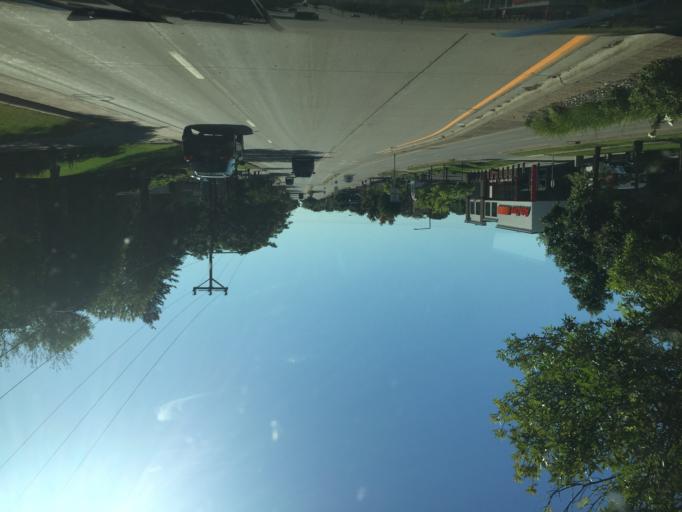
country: US
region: Minnesota
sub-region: Ramsey County
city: Falcon Heights
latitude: 44.9919
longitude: -93.1537
